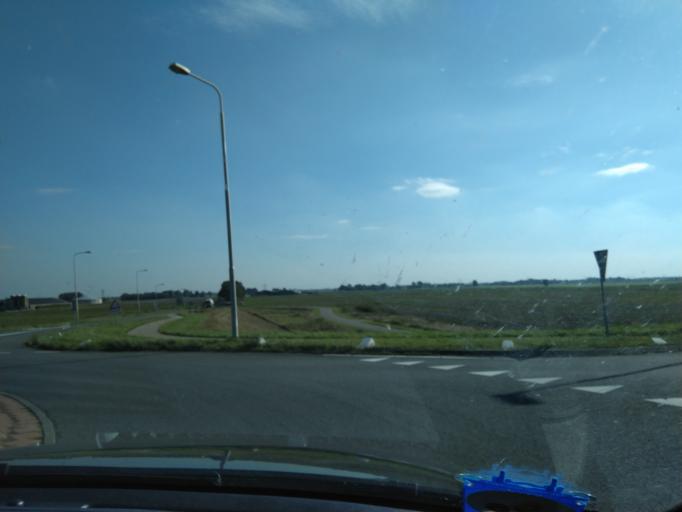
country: NL
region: Groningen
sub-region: Gemeente Veendam
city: Veendam
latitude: 53.0767
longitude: 6.8823
